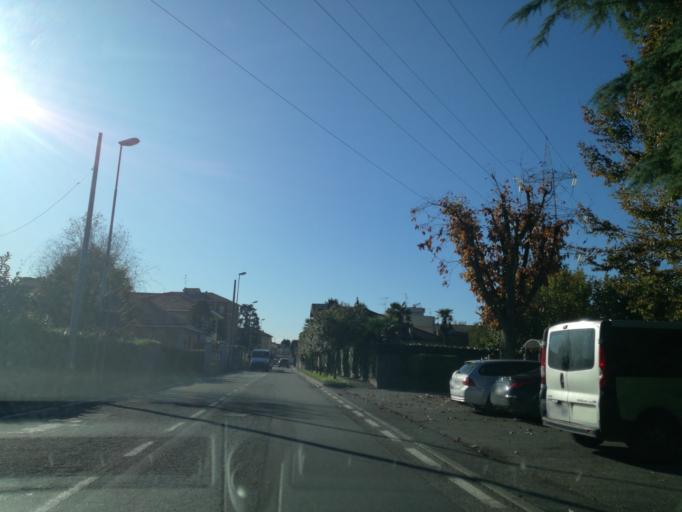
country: IT
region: Lombardy
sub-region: Provincia di Monza e Brianza
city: Macherio
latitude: 45.6358
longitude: 9.2748
